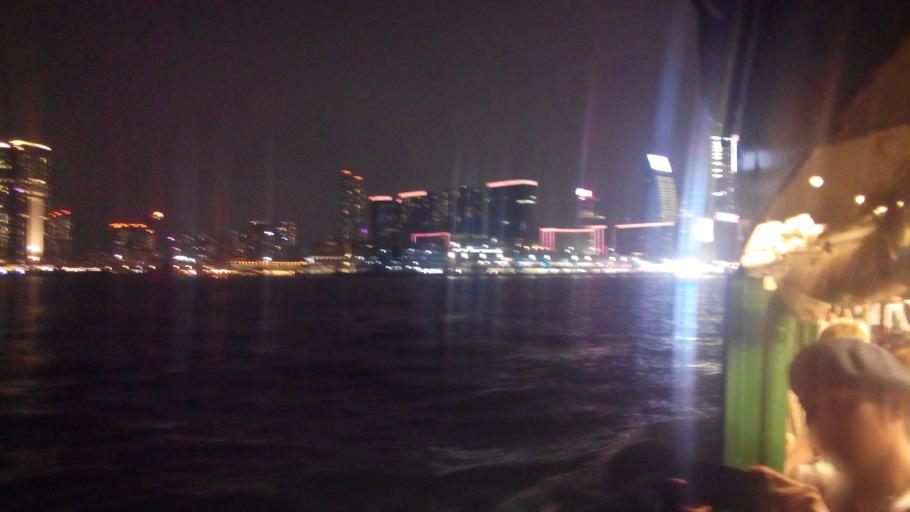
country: HK
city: Hong Kong
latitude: 22.2899
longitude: 114.1622
